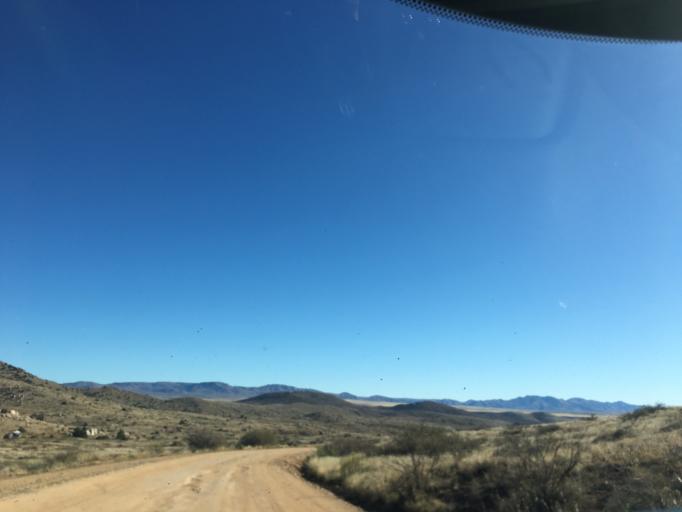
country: US
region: Arizona
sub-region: Yavapai County
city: Cordes Lakes
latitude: 34.2819
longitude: -112.1171
